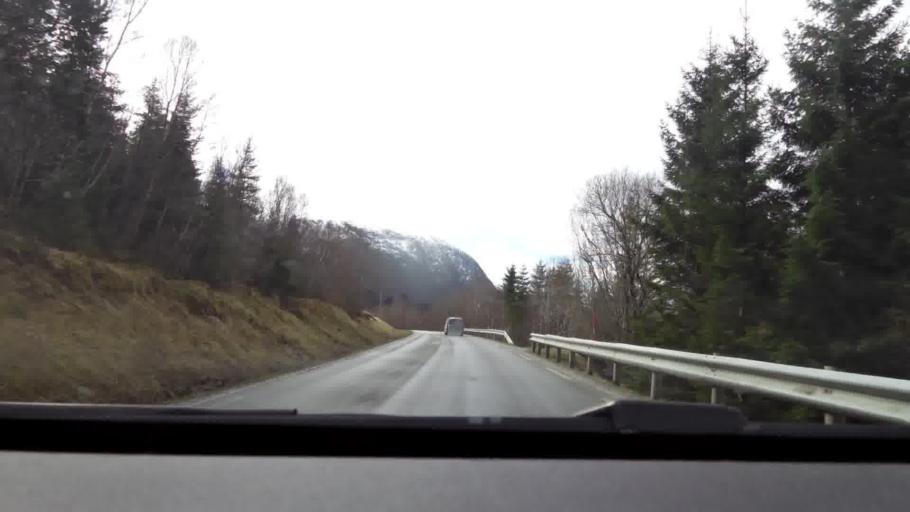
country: NO
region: More og Romsdal
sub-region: Gjemnes
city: Batnfjordsora
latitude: 62.9391
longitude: 7.6063
